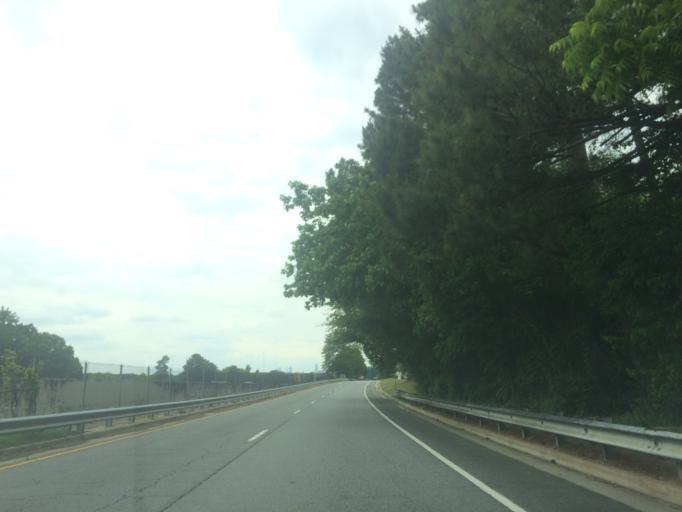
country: US
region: Georgia
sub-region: DeKalb County
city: Chamblee
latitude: 33.8558
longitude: -84.2963
